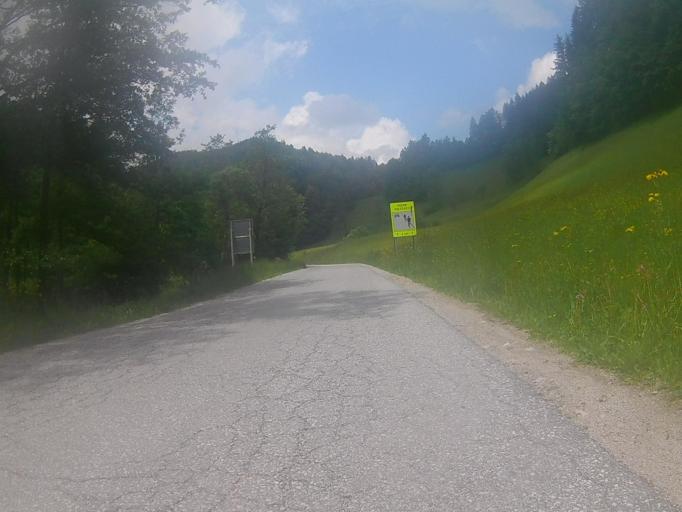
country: SI
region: Maribor
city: Bresternica
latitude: 46.6083
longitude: 15.5506
